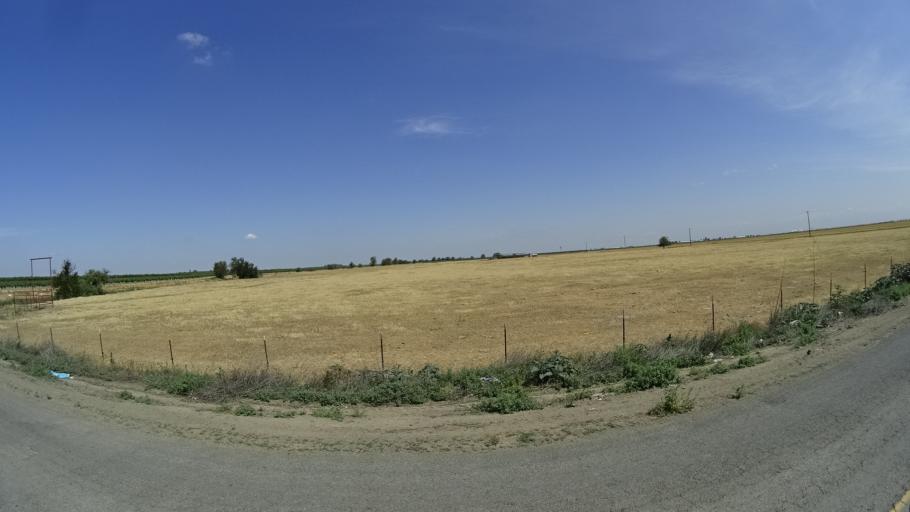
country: US
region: California
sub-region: Kings County
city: Home Garden
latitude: 36.2694
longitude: -119.5534
